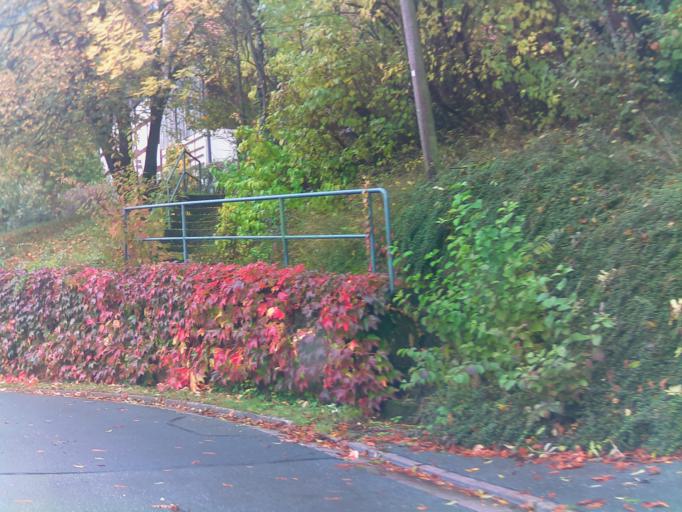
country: DE
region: Bavaria
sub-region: Upper Franconia
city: Schesslitz
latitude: 50.0176
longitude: 11.0260
